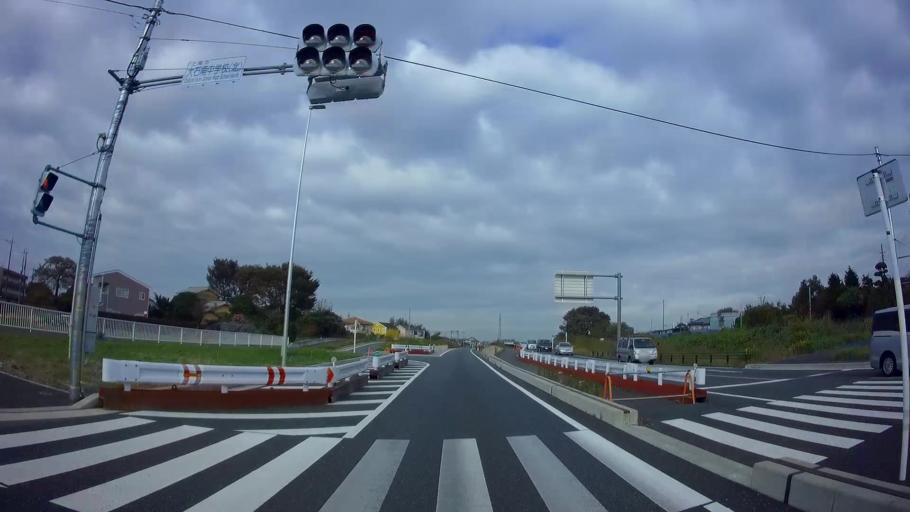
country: JP
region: Saitama
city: Okegawa
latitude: 35.9638
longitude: 139.5543
